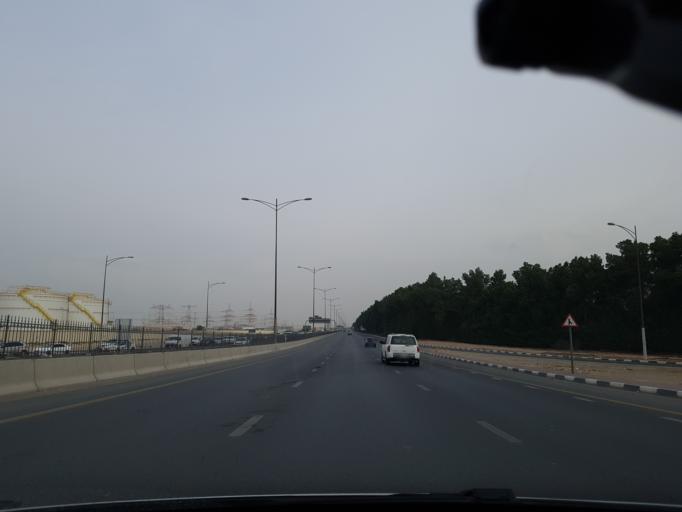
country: AE
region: Ajman
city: Ajman
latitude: 25.3718
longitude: 55.4570
